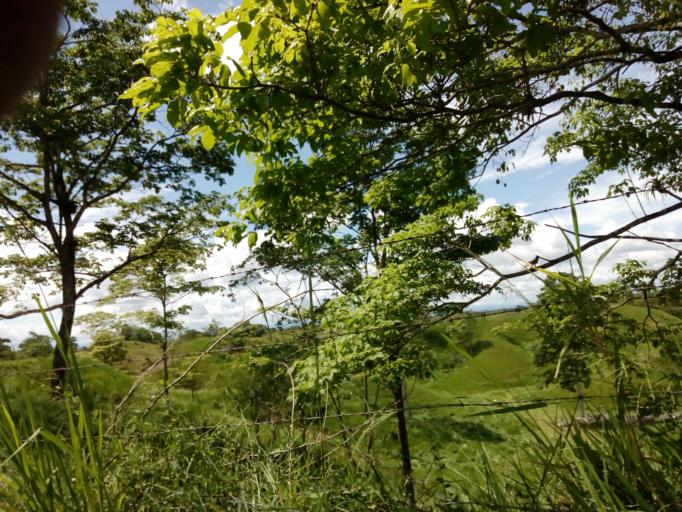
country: CO
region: Boyaca
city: Puerto Boyaca
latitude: 5.9627
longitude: -74.4531
